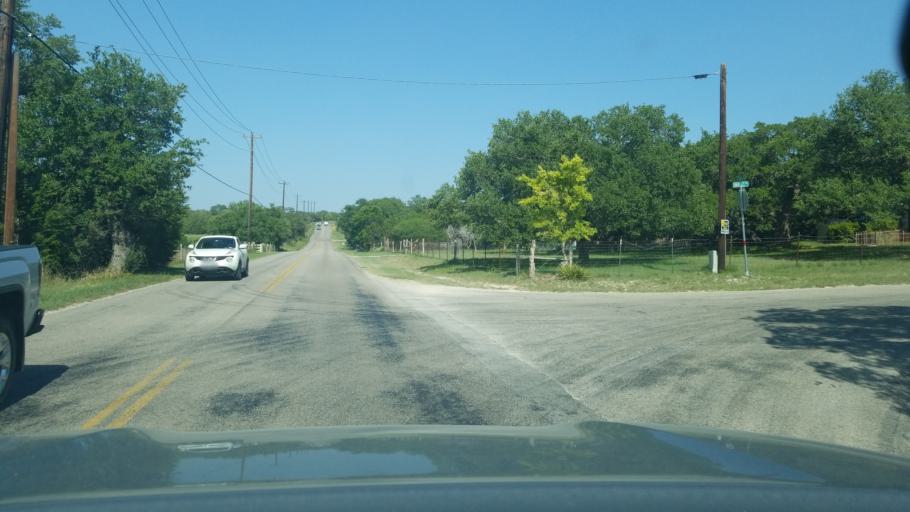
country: US
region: Texas
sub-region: Comal County
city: Bulverde
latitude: 29.7692
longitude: -98.5180
